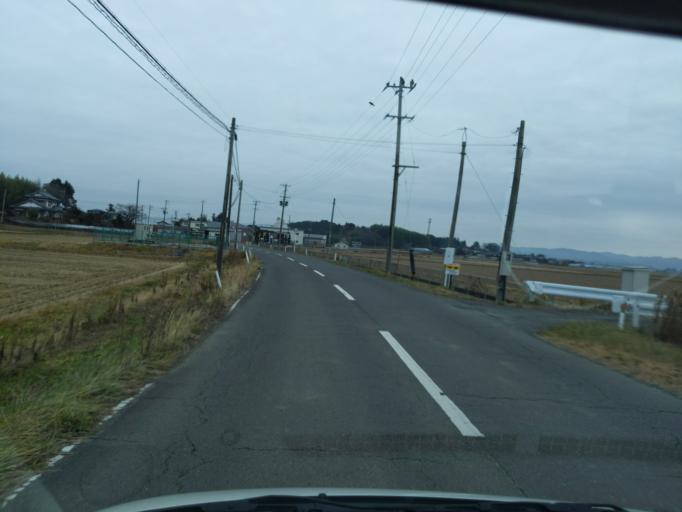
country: JP
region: Miyagi
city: Wakuya
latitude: 38.7252
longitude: 141.2211
